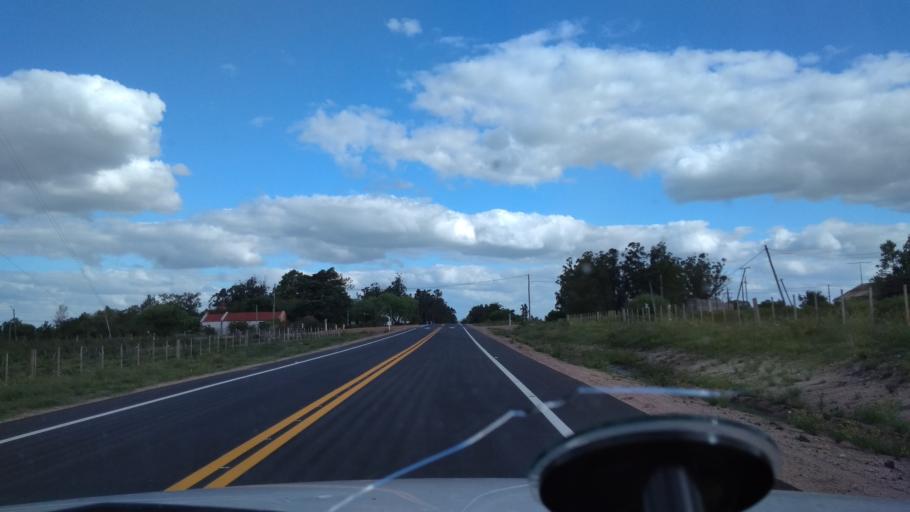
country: UY
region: Florida
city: Casupa
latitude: -33.9992
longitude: -55.6502
